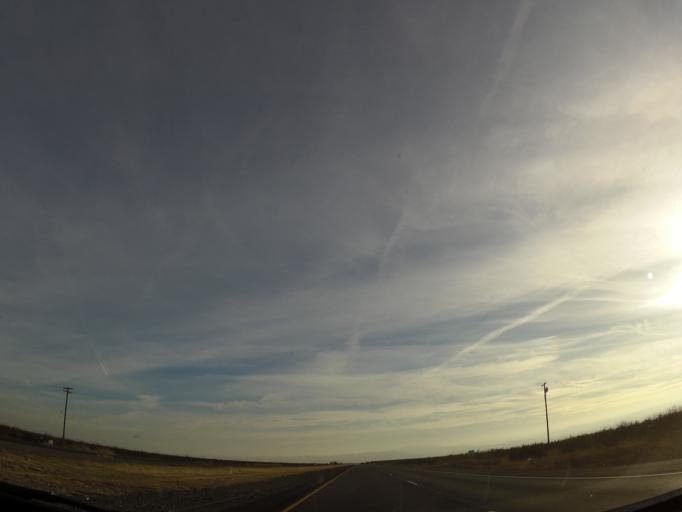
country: US
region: California
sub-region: San Joaquin County
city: Tracy
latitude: 37.7336
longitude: -121.3438
